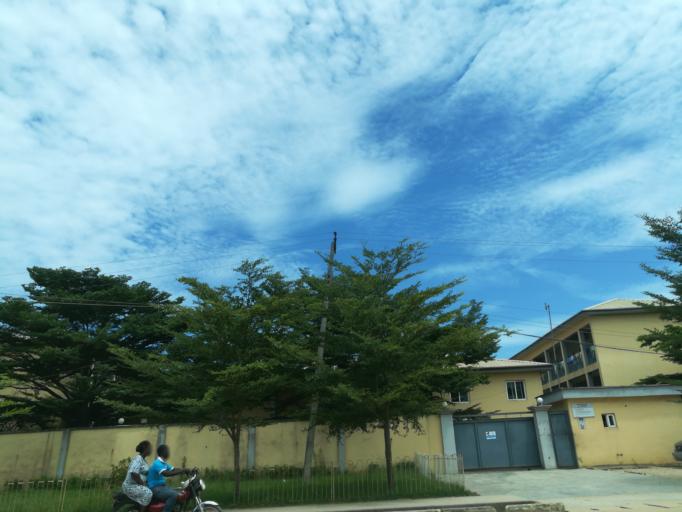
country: NG
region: Lagos
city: Ebute Ikorodu
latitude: 6.5654
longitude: 3.4776
